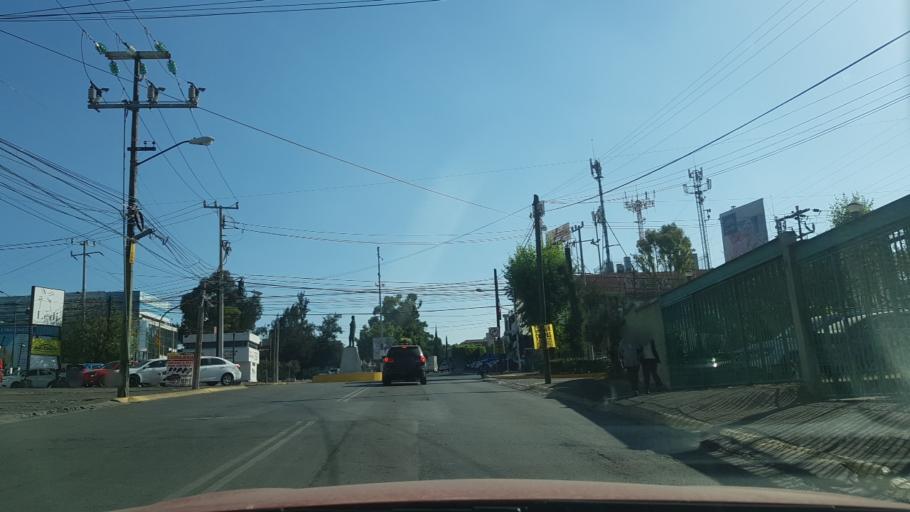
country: MX
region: Mexico
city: Cuautitlan Izcalli
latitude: 19.6450
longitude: -99.2002
